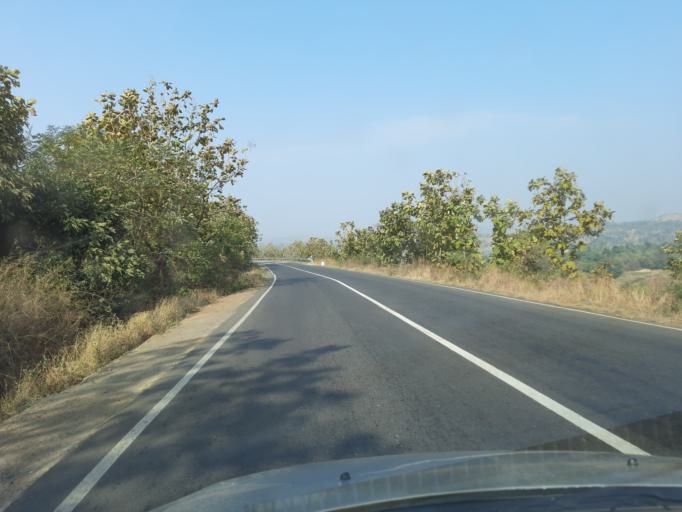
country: IN
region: Maharashtra
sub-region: Nashik Division
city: Surgana
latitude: 20.2568
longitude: 73.6088
